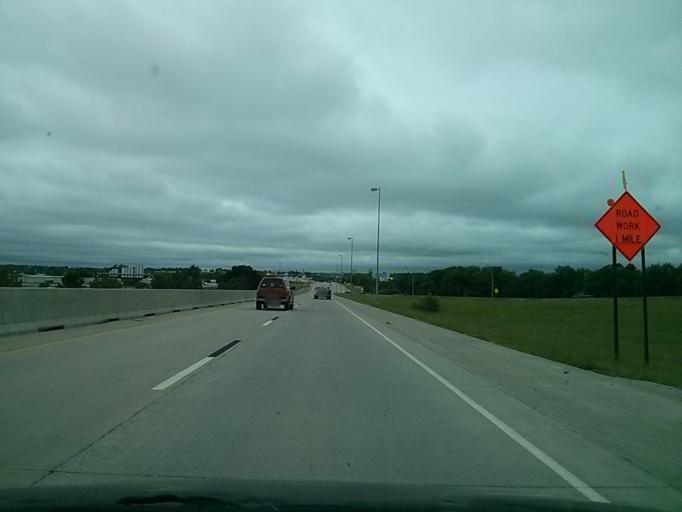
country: US
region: Oklahoma
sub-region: Tulsa County
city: Owasso
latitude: 36.1656
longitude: -95.8619
